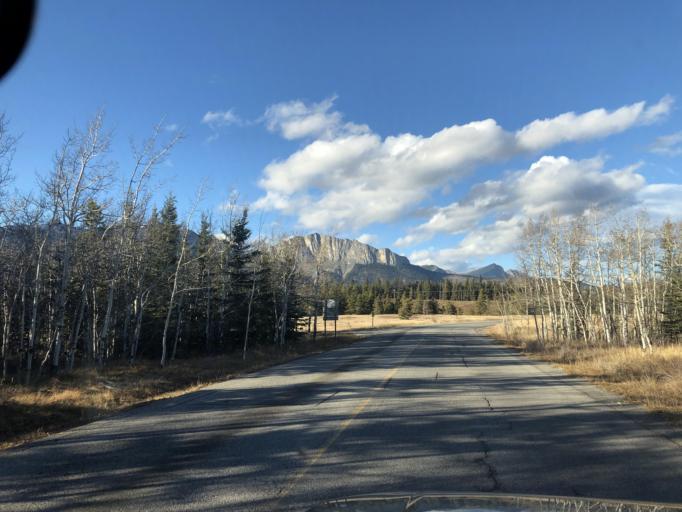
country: CA
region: Alberta
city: Canmore
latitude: 51.0822
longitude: -115.0642
